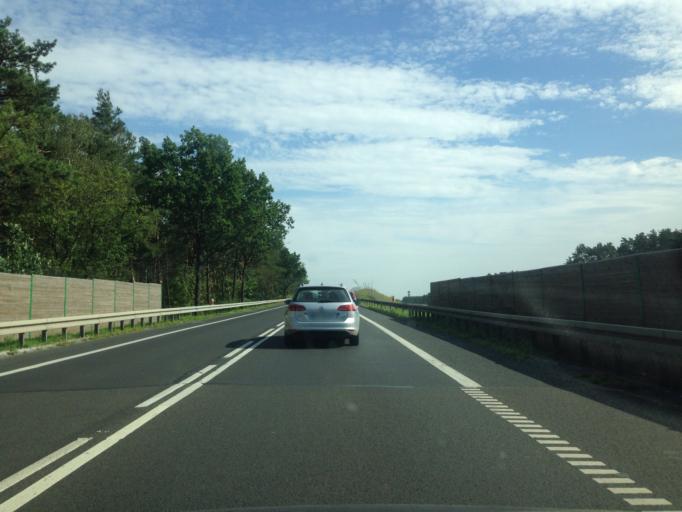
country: PL
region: Kujawsko-Pomorskie
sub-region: Powiat aleksandrowski
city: Aleksandrow Kujawski
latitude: 52.9162
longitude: 18.7154
